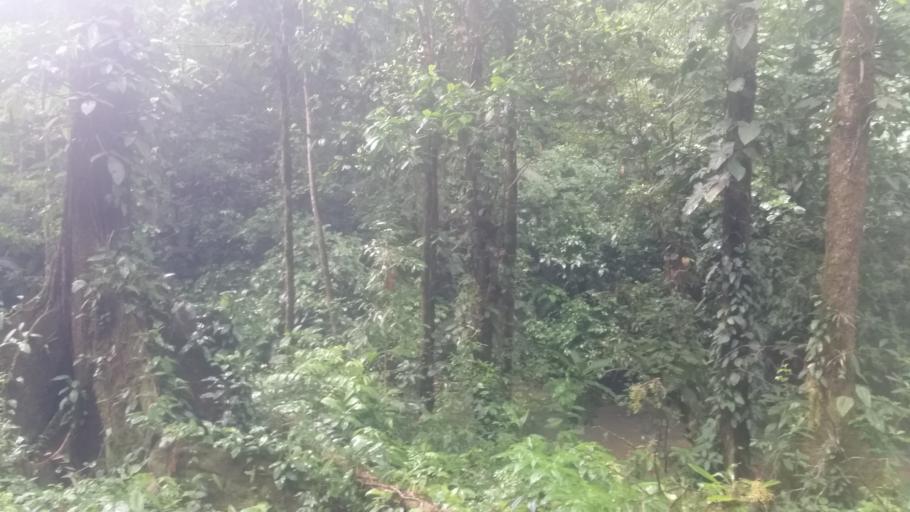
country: NI
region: Atlantico Norte (RAAN)
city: Bonanza
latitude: 14.0248
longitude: -84.7471
